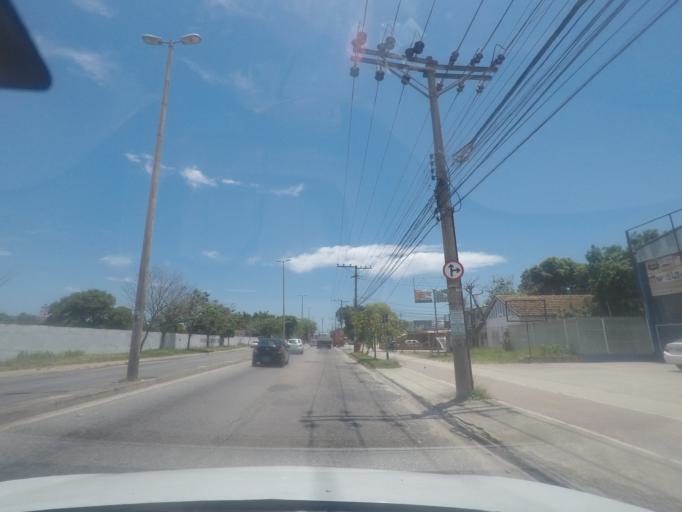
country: BR
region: Rio de Janeiro
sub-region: Itaguai
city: Itaguai
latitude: -22.9077
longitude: -43.6856
